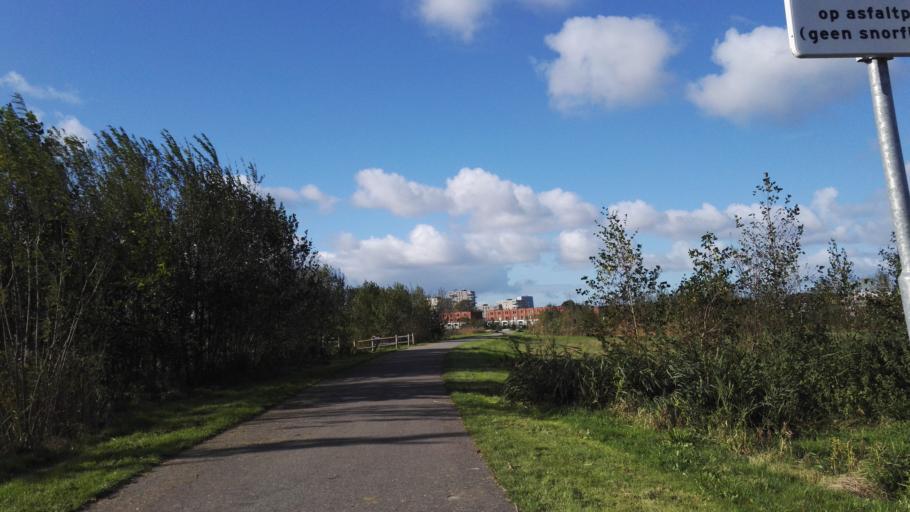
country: NL
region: Gelderland
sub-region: Gemeente Apeldoorn
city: Apeldoorn
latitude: 52.2346
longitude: 6.0076
